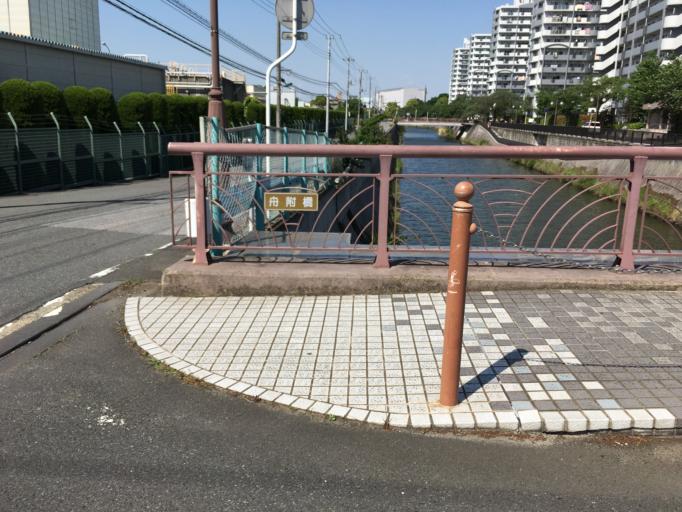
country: JP
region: Chiba
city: Matsudo
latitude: 35.8042
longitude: 139.9129
